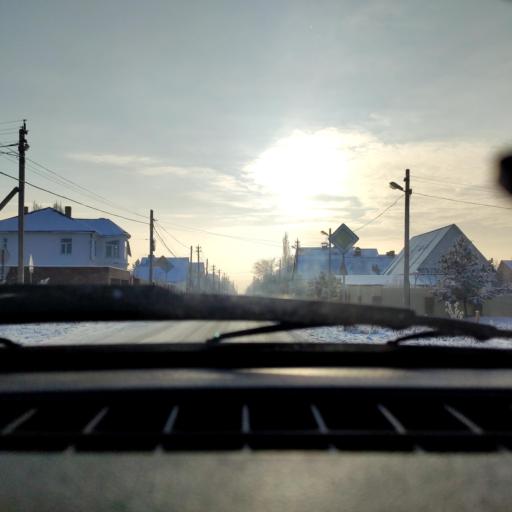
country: RU
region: Bashkortostan
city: Ufa
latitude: 54.6013
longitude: 55.9355
